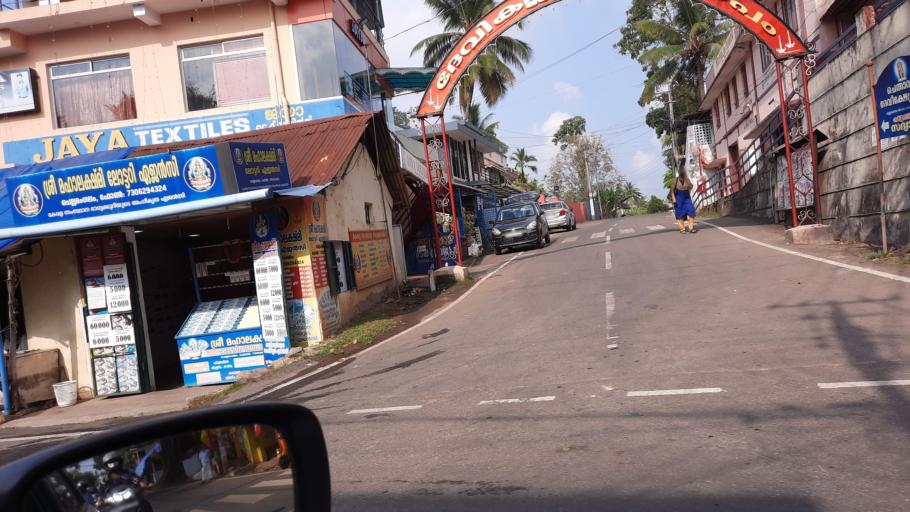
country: IN
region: Kerala
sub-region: Thiruvananthapuram
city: Thiruvananthapuram
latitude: 8.5644
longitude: 76.9211
